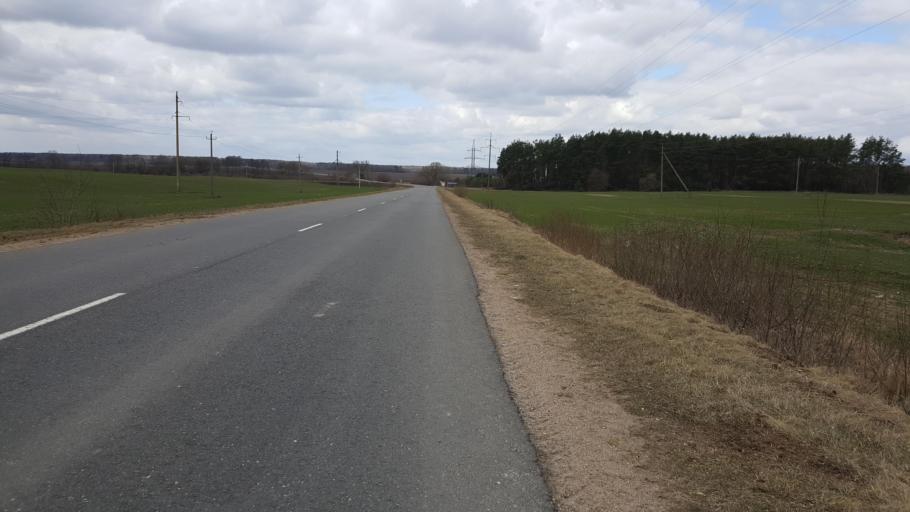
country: BY
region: Brest
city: Kamyanyets
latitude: 52.3802
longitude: 23.6610
